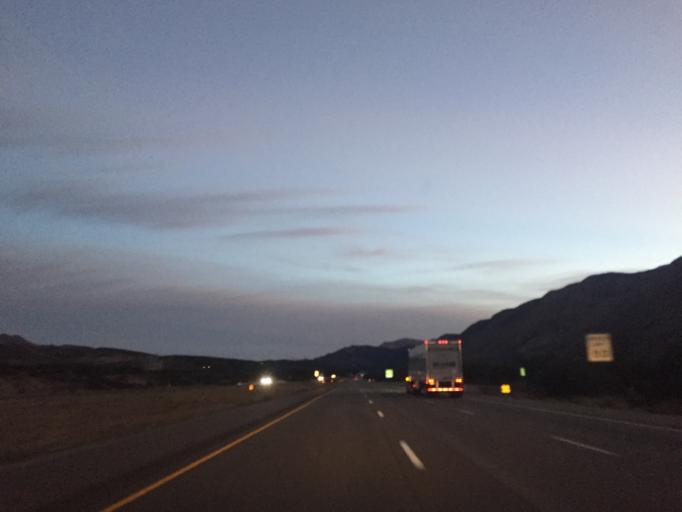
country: US
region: Utah
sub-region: Washington County
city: Toquerville
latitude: 37.3293
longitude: -113.2831
